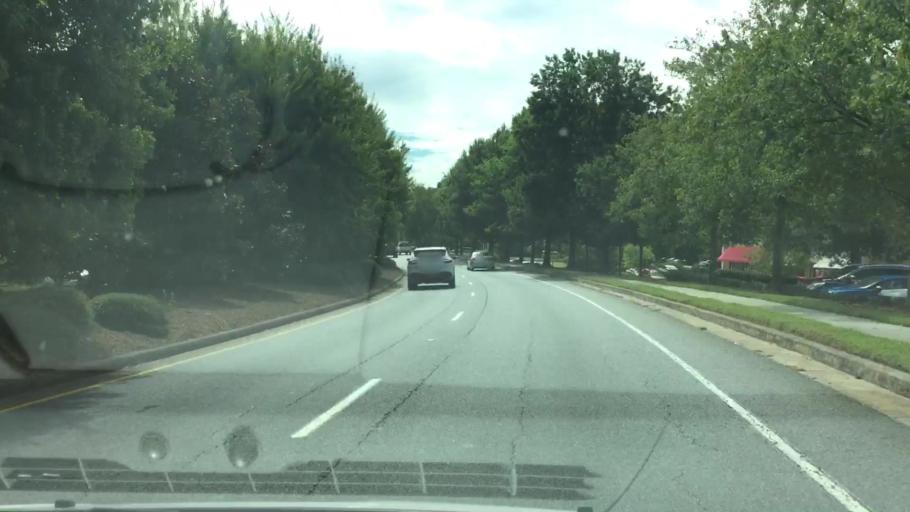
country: US
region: Georgia
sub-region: Fulton County
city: Alpharetta
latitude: 34.0896
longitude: -84.2747
